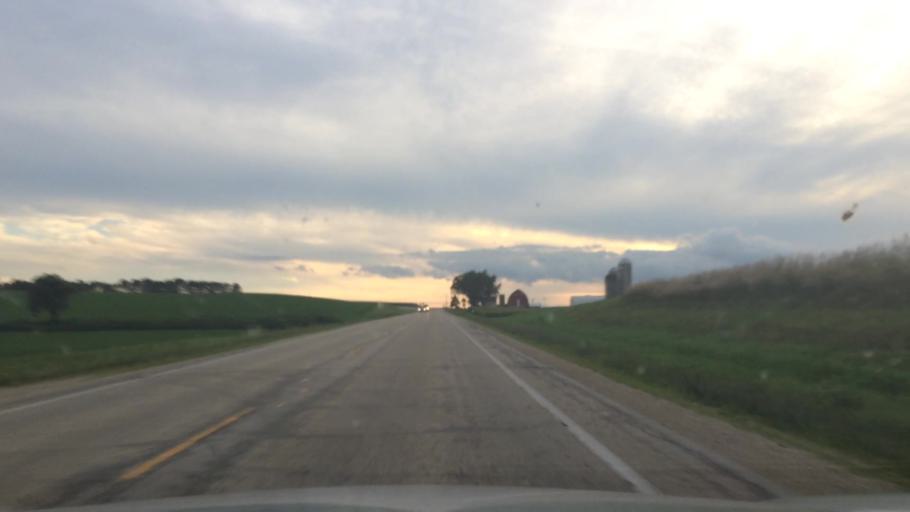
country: US
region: Wisconsin
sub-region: Columbia County
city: Lodi
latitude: 43.2357
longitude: -89.5339
